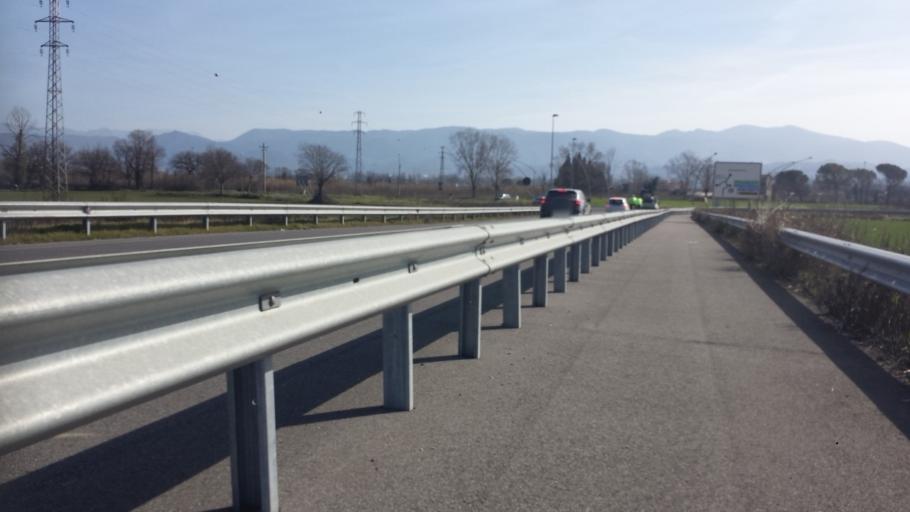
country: IT
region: Umbria
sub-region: Provincia di Terni
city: Terni
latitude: 42.5731
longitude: 12.6005
